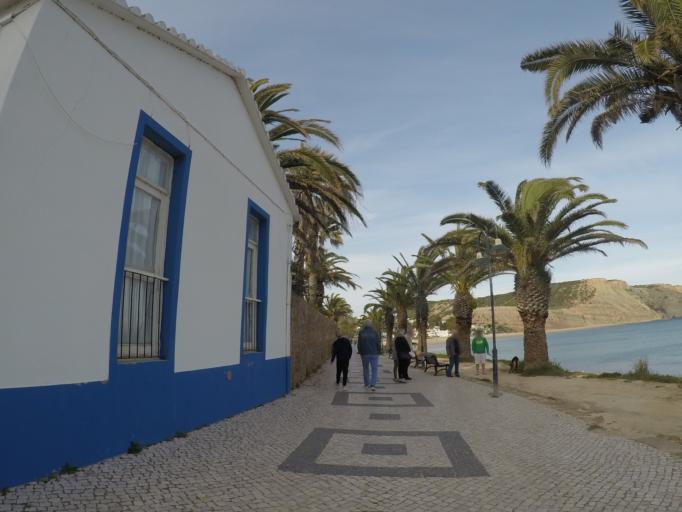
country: PT
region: Faro
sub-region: Lagos
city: Lagos
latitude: 37.0853
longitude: -8.7296
